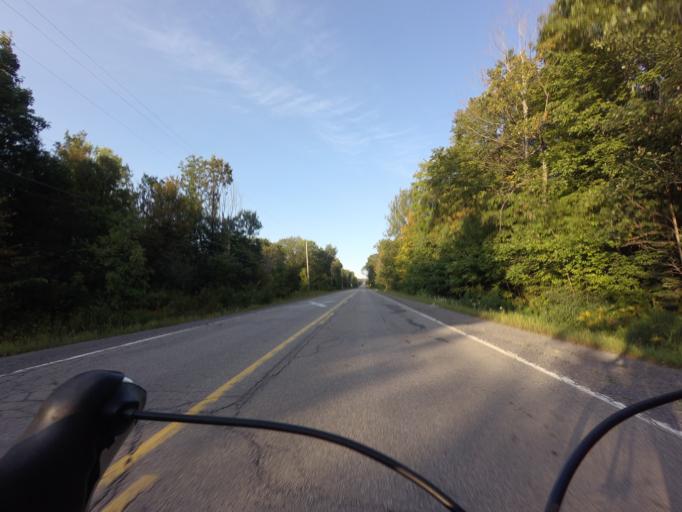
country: CA
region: Ontario
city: Bells Corners
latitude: 45.3822
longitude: -75.9485
